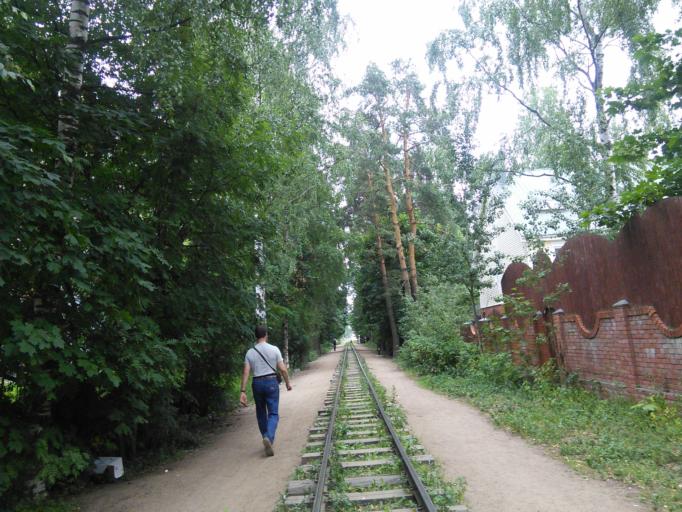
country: RU
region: St.-Petersburg
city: Kolomyagi
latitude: 60.0300
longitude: 30.2926
